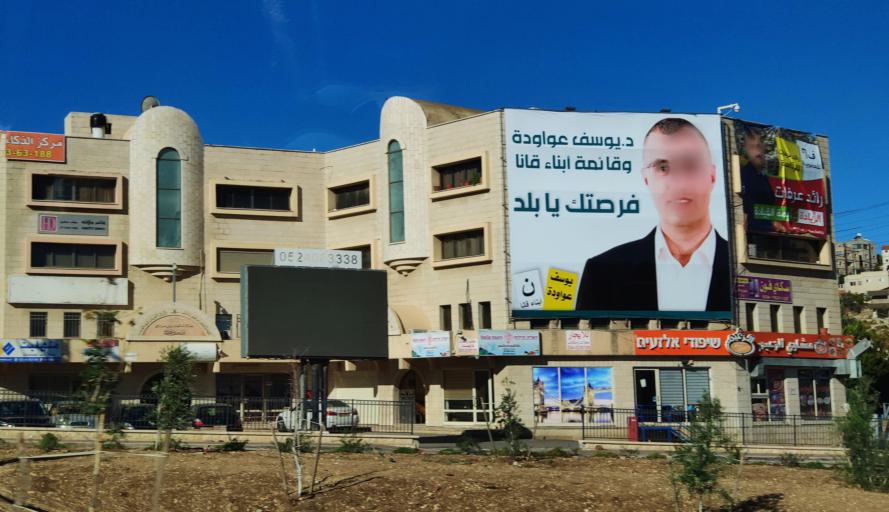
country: IL
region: Northern District
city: Er Reina
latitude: 32.7352
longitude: 35.3255
